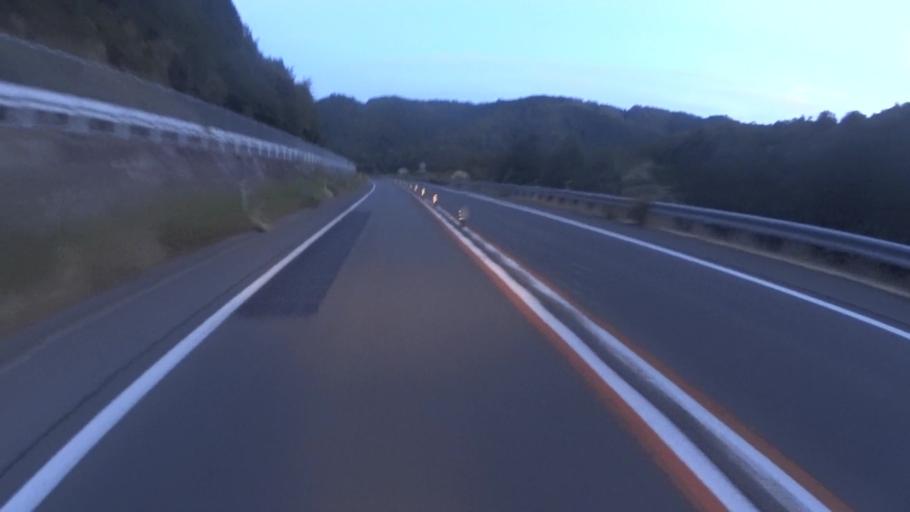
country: JP
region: Kyoto
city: Kameoka
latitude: 35.1333
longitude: 135.4567
